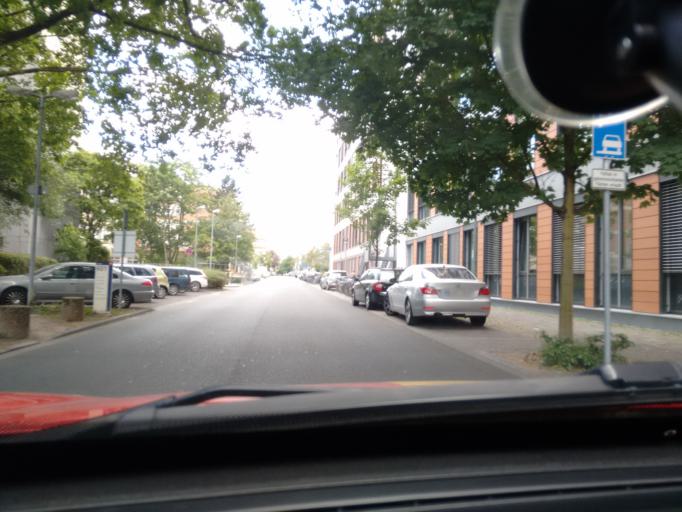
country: DE
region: Rheinland-Pfalz
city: Mainz
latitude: 49.9942
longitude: 8.2573
